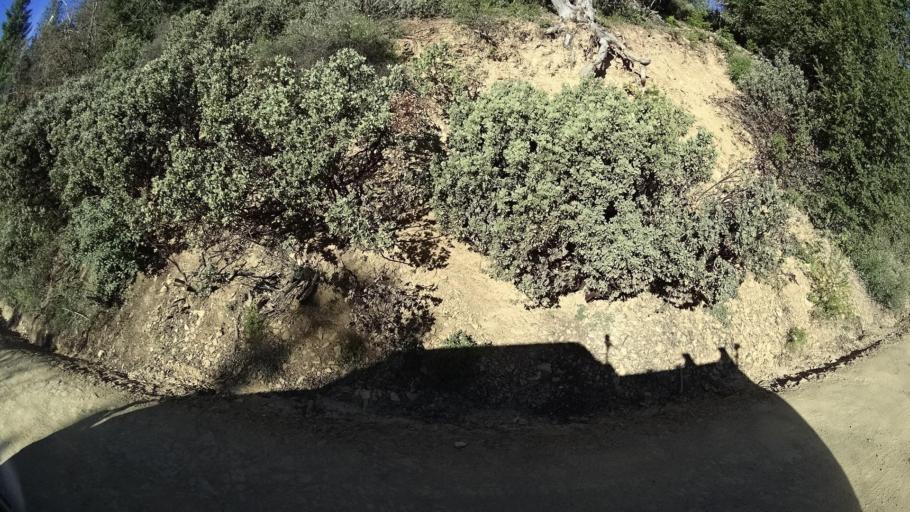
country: US
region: California
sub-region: Lake County
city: Upper Lake
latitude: 39.3182
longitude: -122.9456
